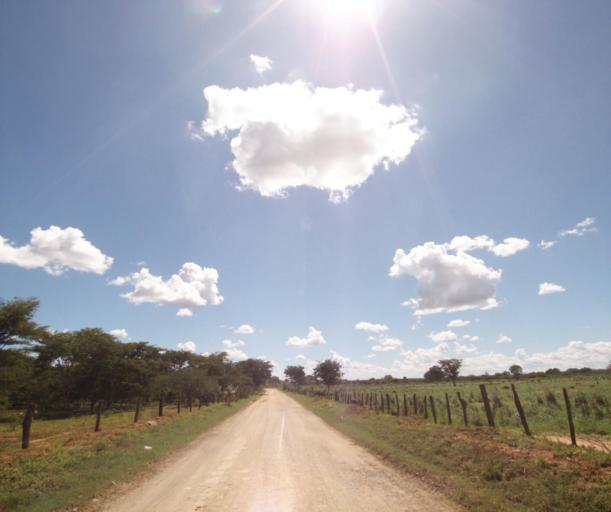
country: BR
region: Bahia
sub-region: Carinhanha
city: Carinhanha
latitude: -14.2218
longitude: -44.2957
